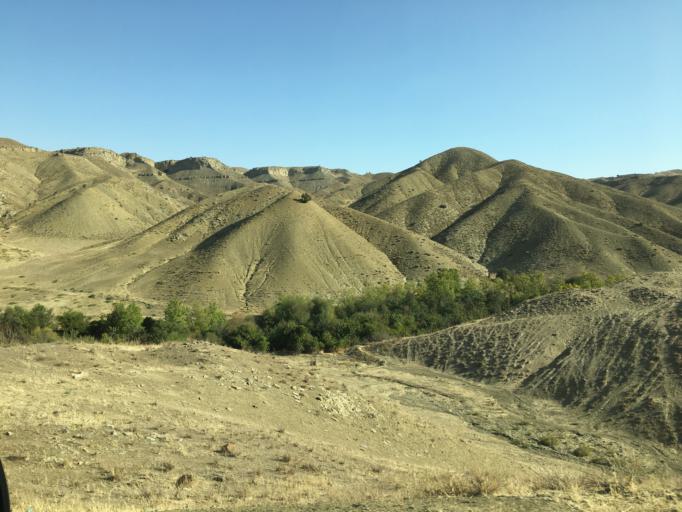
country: TM
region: Balkan
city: Magtymguly
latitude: 38.3021
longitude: 56.7744
